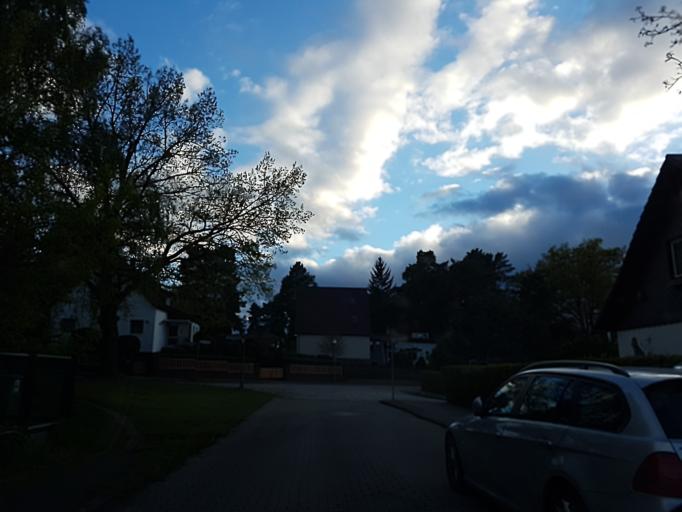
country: DE
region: Berlin
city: Waidmannslust
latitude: 52.6118
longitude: 13.3277
